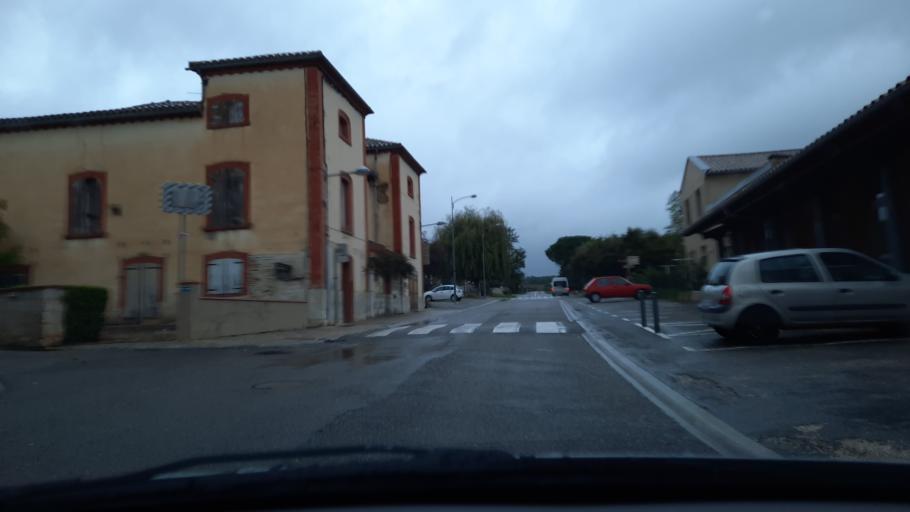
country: FR
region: Midi-Pyrenees
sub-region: Departement du Tarn-et-Garonne
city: Lafrancaise
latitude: 44.1904
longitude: 1.2851
